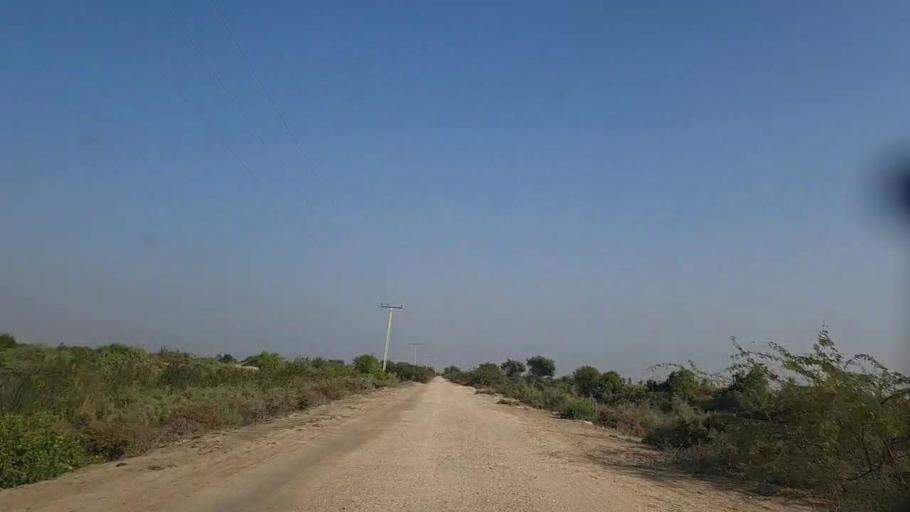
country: PK
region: Sindh
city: Jati
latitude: 24.4602
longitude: 68.3014
